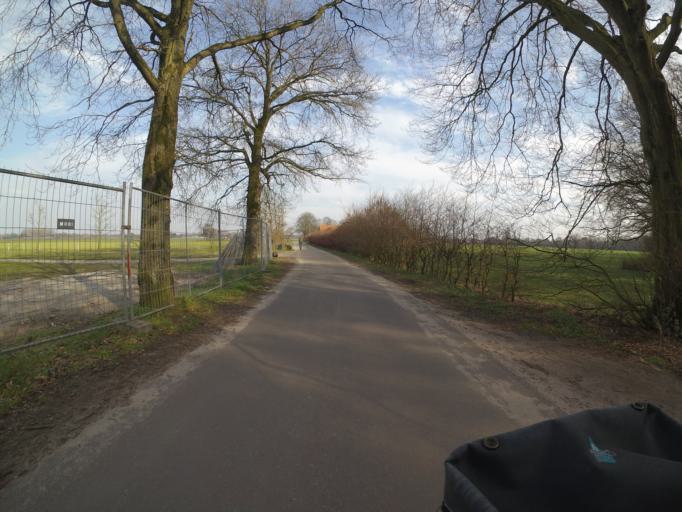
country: NL
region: North Brabant
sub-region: Gemeente Dongen
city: Dongen
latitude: 51.6021
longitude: 4.9054
